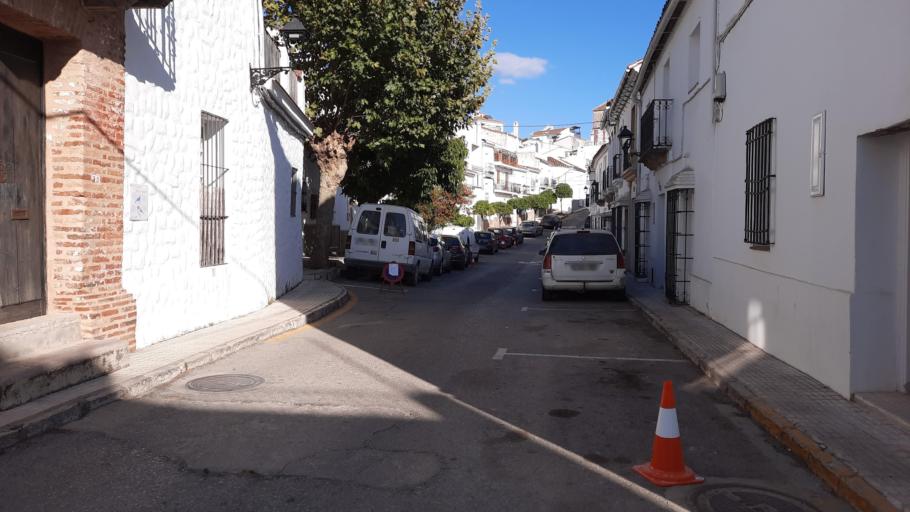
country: ES
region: Andalusia
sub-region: Provincia de Malaga
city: Gaucin
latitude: 36.5179
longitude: -5.3165
